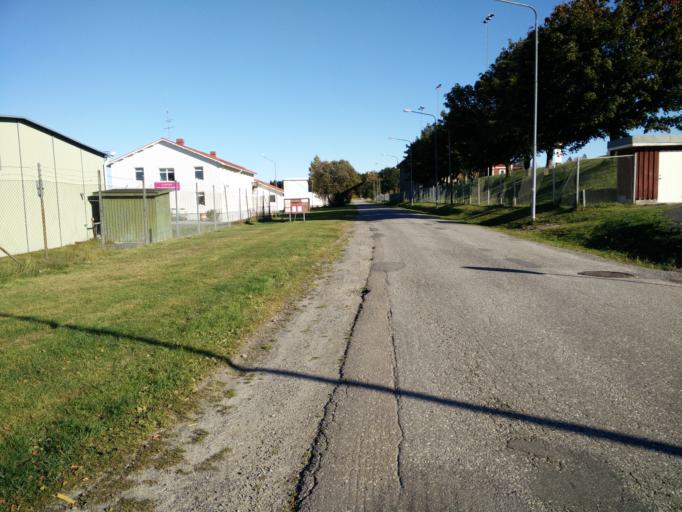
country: SE
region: Vaesternorrland
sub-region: Haernoesands Kommun
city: Haernoesand
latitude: 62.6380
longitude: 17.9631
